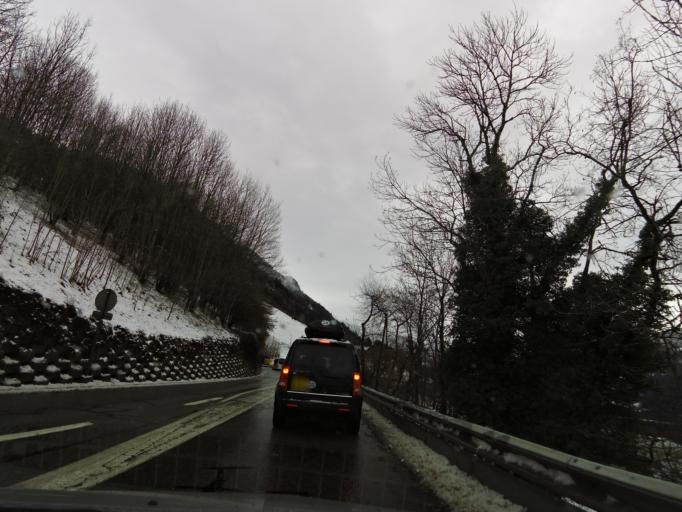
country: FR
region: Rhone-Alpes
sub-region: Departement de la Haute-Savoie
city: Taninges
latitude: 46.1127
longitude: 6.6061
